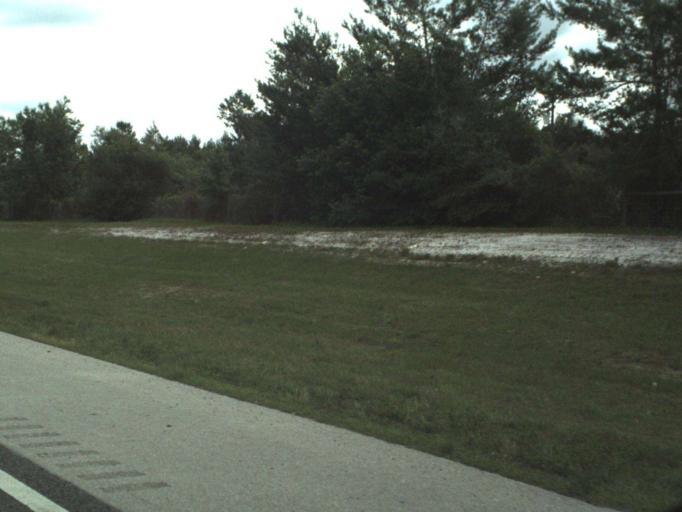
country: US
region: Florida
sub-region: Volusia County
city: Lake Helen
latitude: 29.0073
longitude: -81.2406
